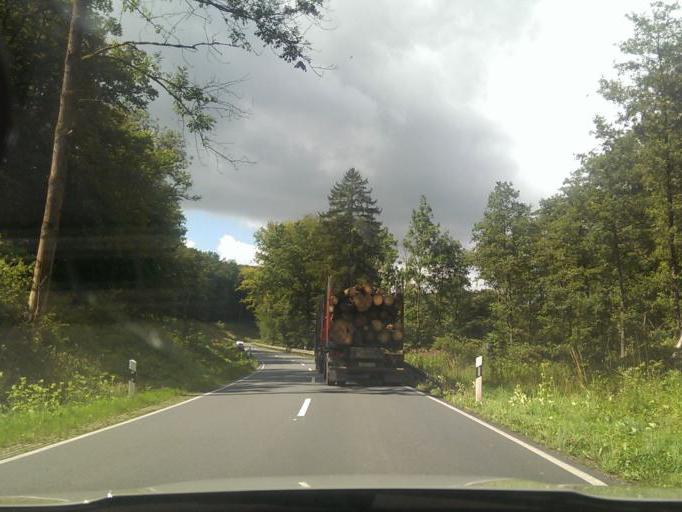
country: DE
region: North Rhine-Westphalia
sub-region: Regierungsbezirk Detmold
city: Hoexter
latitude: 51.8234
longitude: 9.3731
